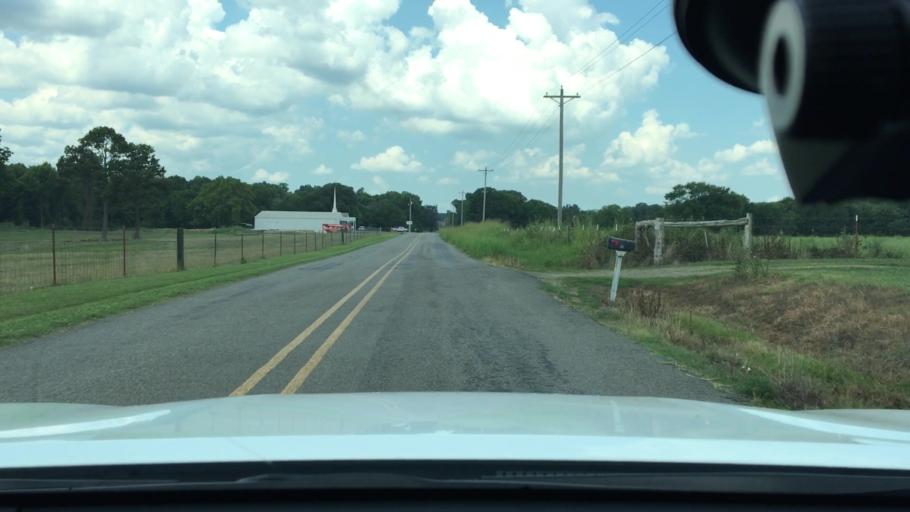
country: US
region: Arkansas
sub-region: Logan County
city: Paris
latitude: 35.2689
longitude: -93.6571
